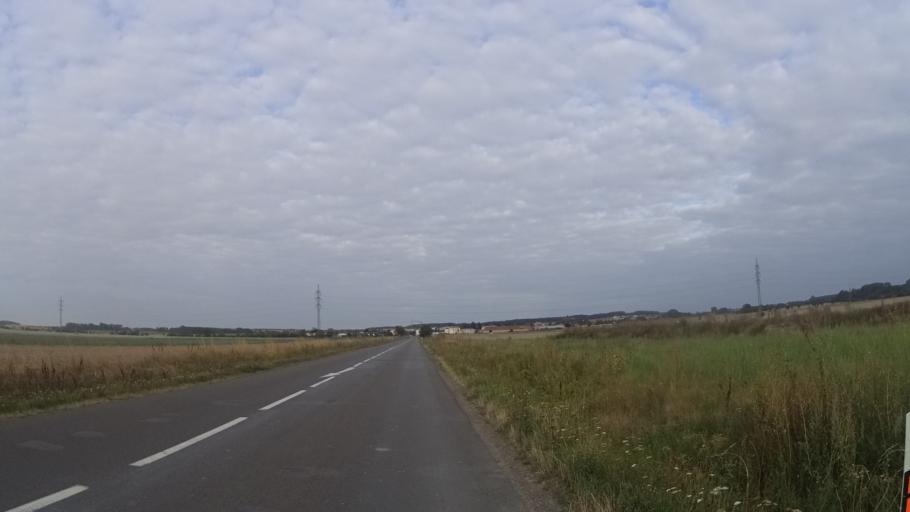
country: CZ
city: Stezery
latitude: 50.2114
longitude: 15.7707
